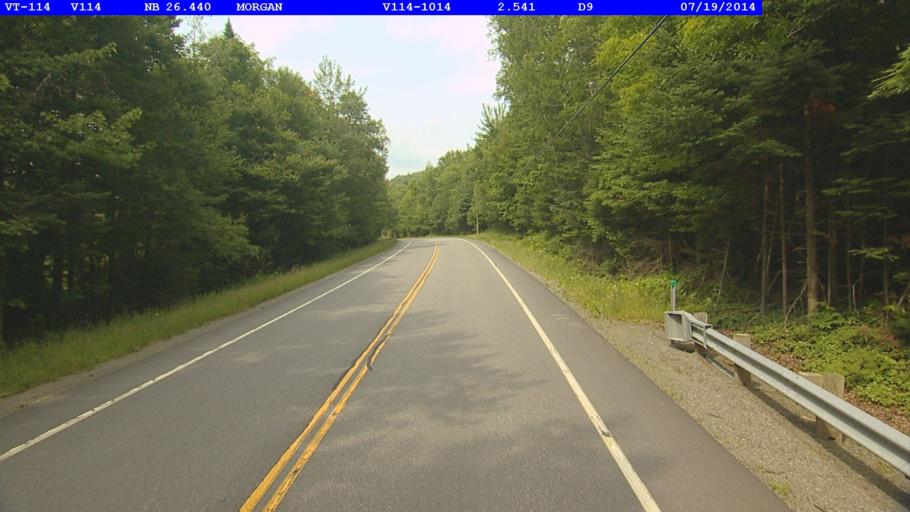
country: CA
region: Quebec
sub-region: Estrie
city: Coaticook
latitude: 44.8804
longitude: -71.8974
